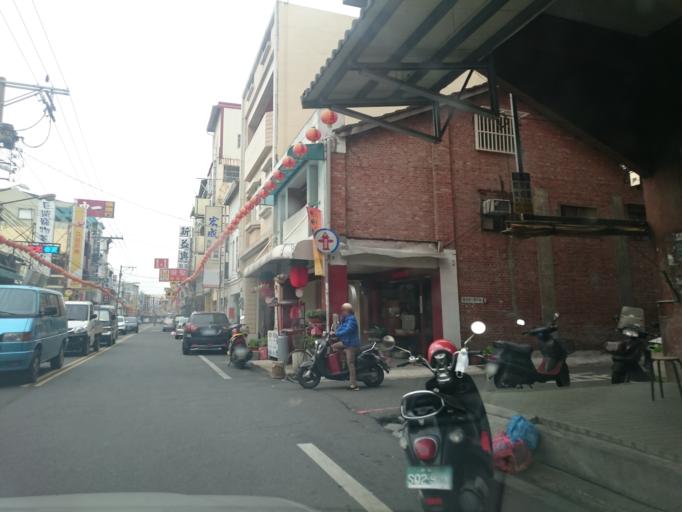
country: TW
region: Taiwan
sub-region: Nantou
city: Nantou
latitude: 23.8608
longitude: 120.5851
